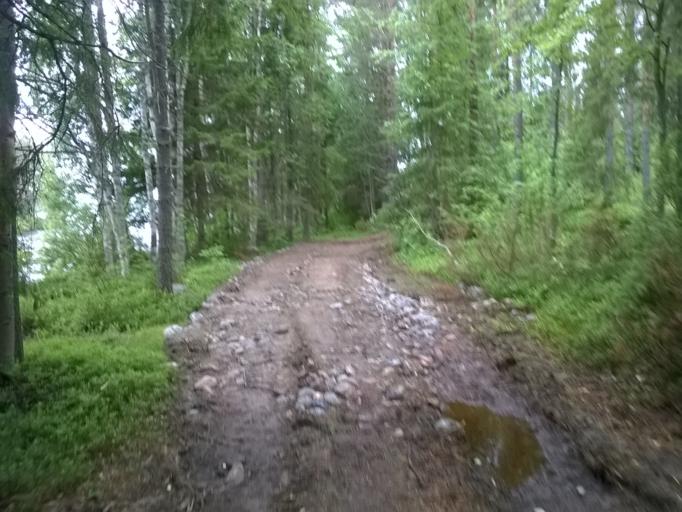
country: FI
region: Kainuu
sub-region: Kehys-Kainuu
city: Kuhmo
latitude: 64.1254
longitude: 29.4010
